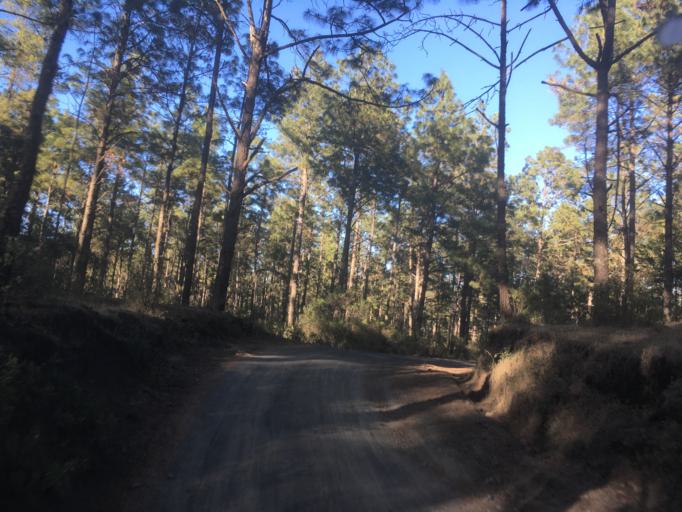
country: MX
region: Michoacan
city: Angahuan
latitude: 19.4636
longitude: -102.2271
